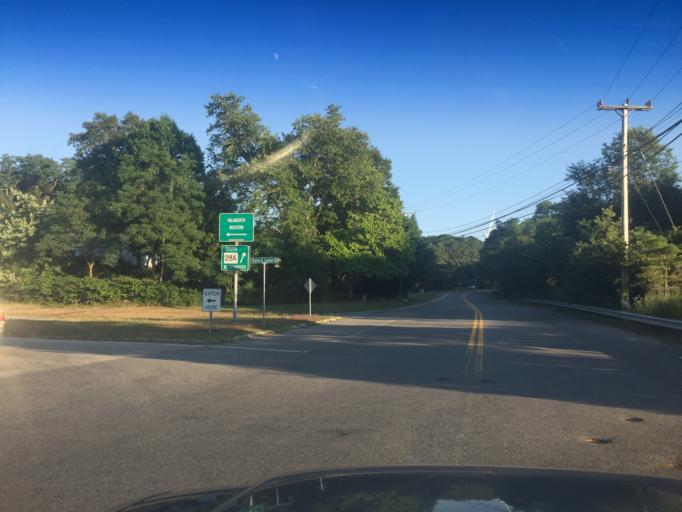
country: US
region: Massachusetts
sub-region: Barnstable County
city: West Falmouth
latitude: 41.6178
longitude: -70.6229
